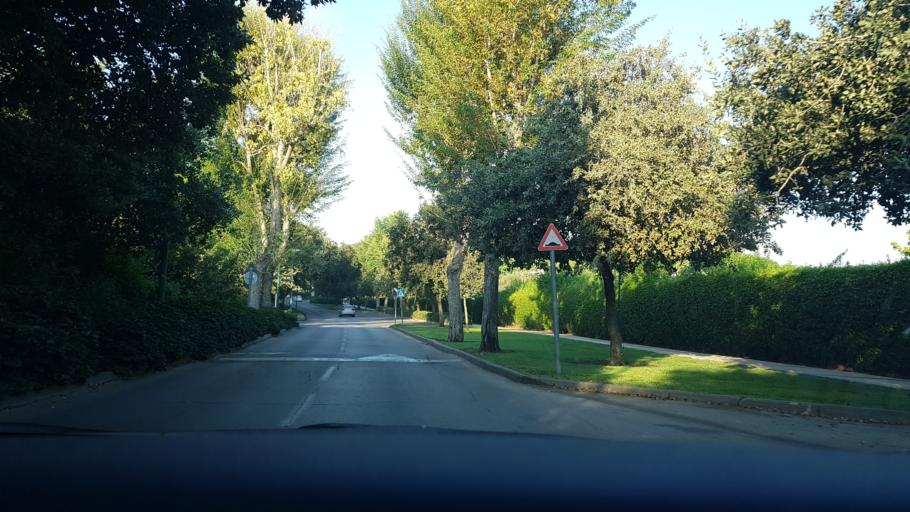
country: IL
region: Central District
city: Ness Ziona
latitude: 31.9081
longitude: 34.8163
